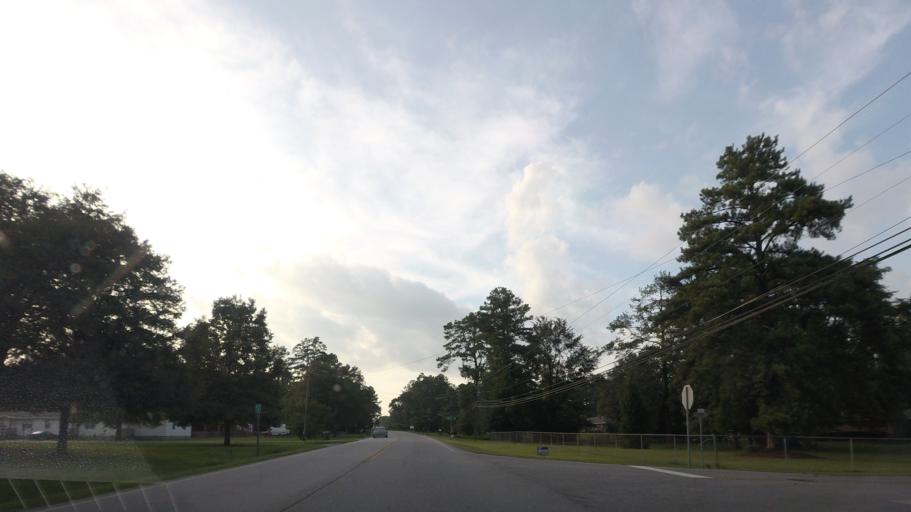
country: US
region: Georgia
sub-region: Wilkinson County
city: Gordon
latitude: 32.8851
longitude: -83.3455
